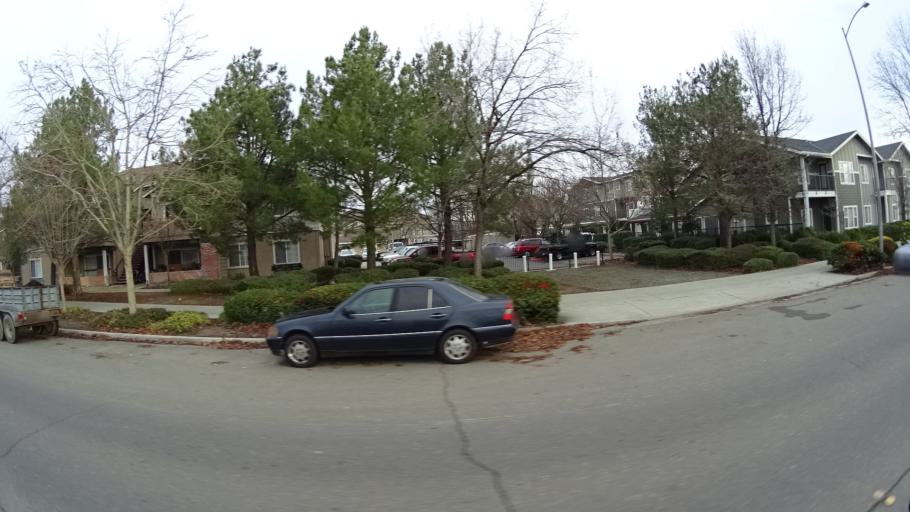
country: US
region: California
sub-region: Yolo County
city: Davis
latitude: 38.5701
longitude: -121.7280
